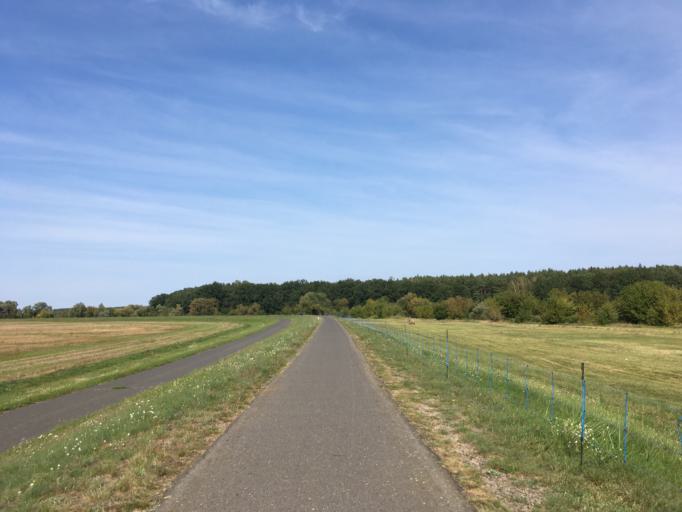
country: PL
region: Lubusz
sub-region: Powiat krosnienski
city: Gubin
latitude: 52.0409
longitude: 14.7486
